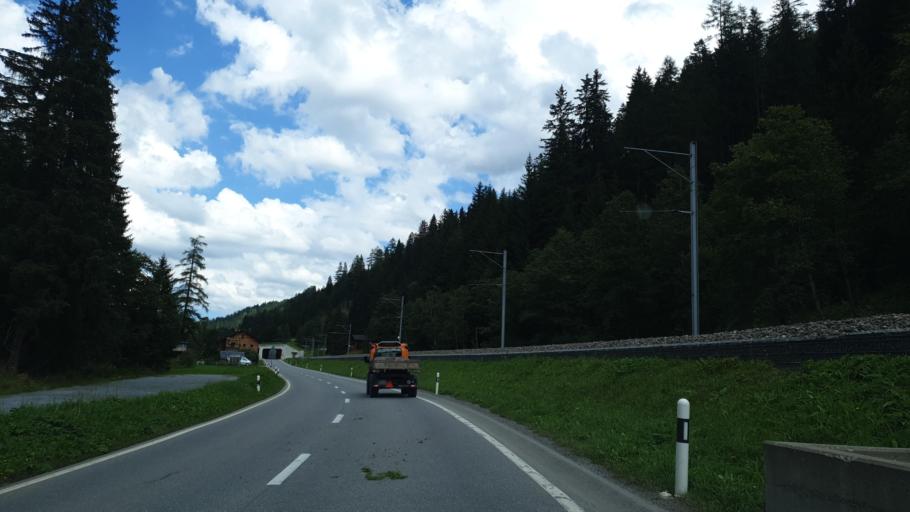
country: CH
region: Grisons
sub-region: Plessur District
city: Arosa
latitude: 46.7198
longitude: 9.7656
